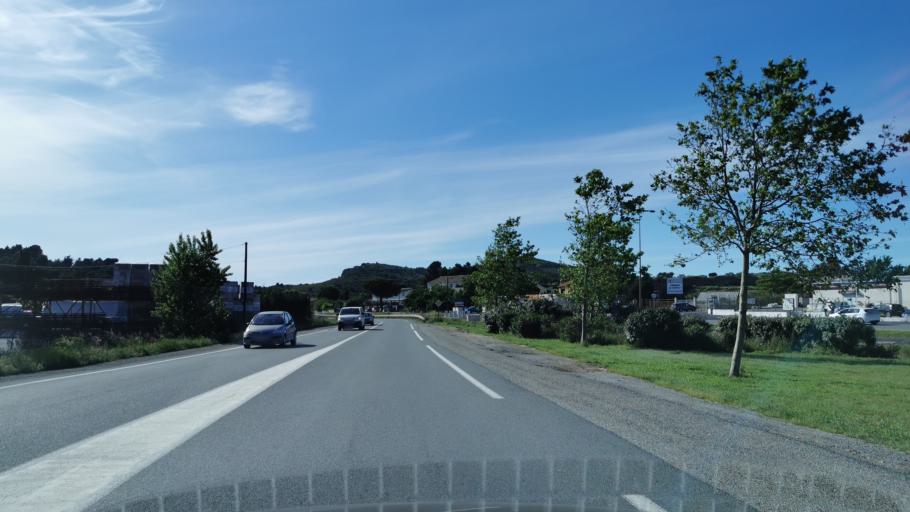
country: FR
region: Languedoc-Roussillon
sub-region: Departement de l'Aude
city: Nevian
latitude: 43.1842
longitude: 2.9328
